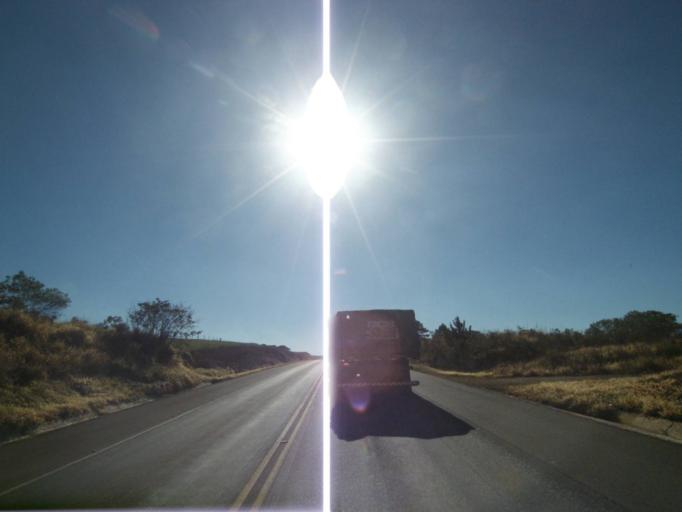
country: BR
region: Parana
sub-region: Tibagi
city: Tibagi
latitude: -24.6458
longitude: -50.4537
